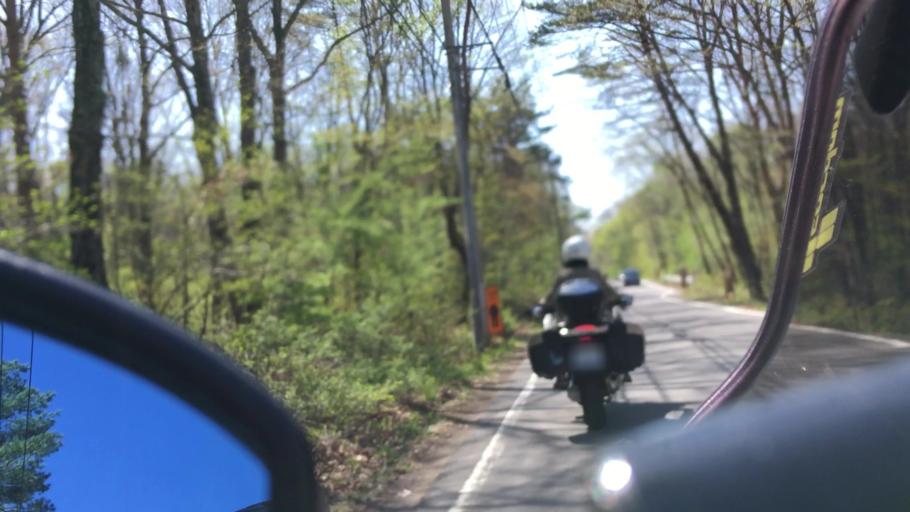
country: JP
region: Nagano
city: Komoro
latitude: 36.4633
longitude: 138.5551
